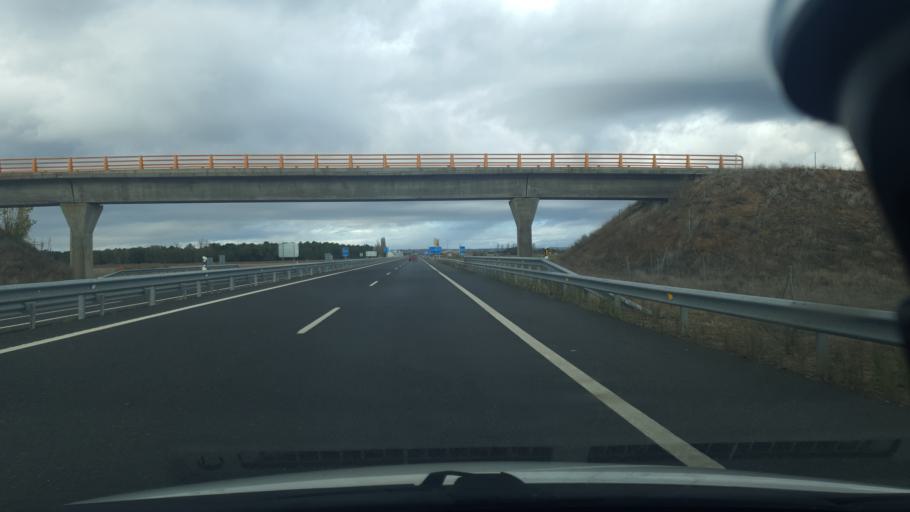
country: ES
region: Castille and Leon
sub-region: Provincia de Segovia
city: Sanchonuno
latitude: 41.3007
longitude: -4.3011
